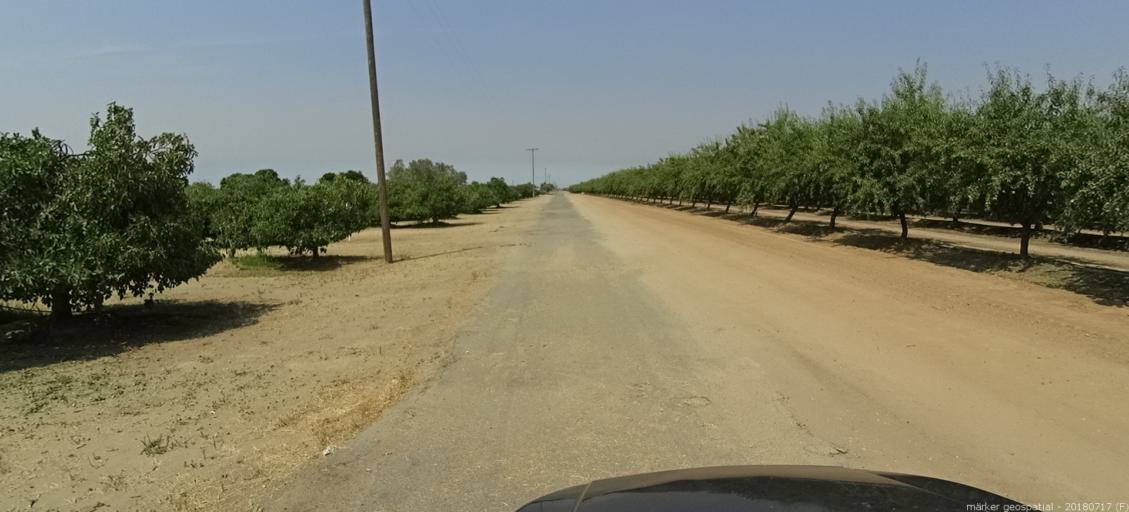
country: US
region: California
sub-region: Madera County
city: Fairmead
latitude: 37.1342
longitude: -120.1402
